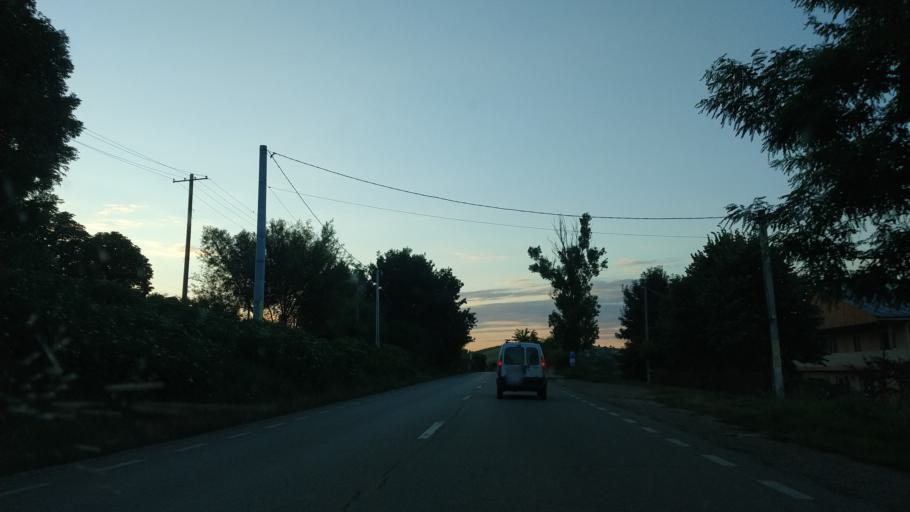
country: RO
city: Vanatori
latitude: 47.2352
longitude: 27.5341
